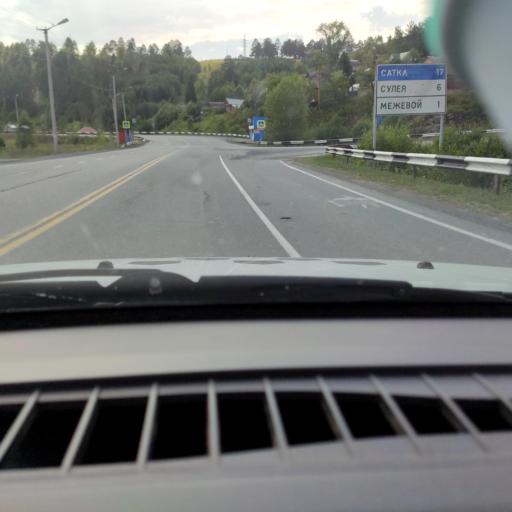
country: RU
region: Chelyabinsk
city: Mezhevoy
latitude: 55.1678
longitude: 58.7944
